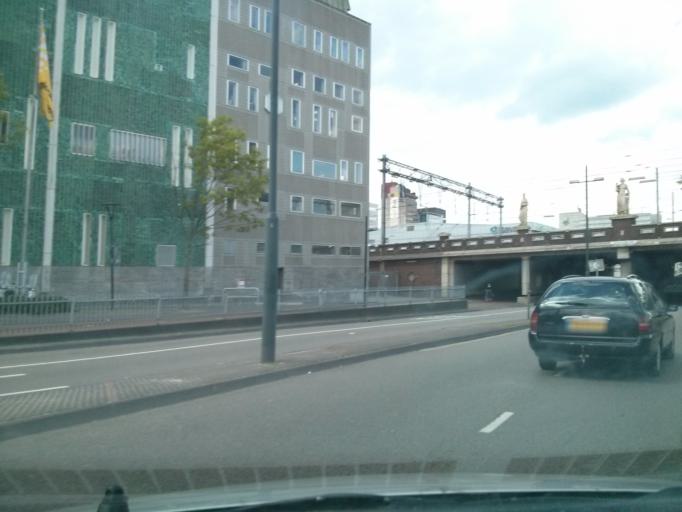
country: NL
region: North Brabant
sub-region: Gemeente Eindhoven
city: Eindhoven
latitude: 51.4419
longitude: 5.4775
